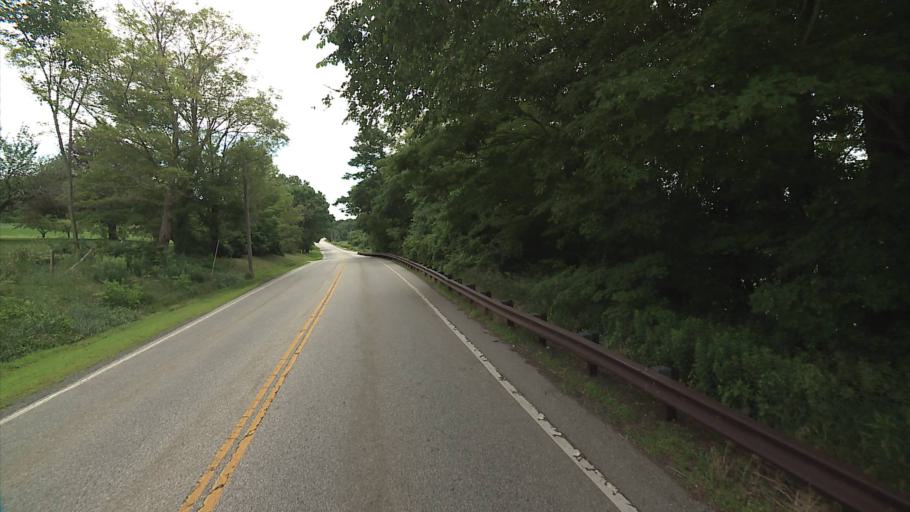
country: US
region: Connecticut
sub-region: New London County
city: Preston City
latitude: 41.5388
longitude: -71.9689
